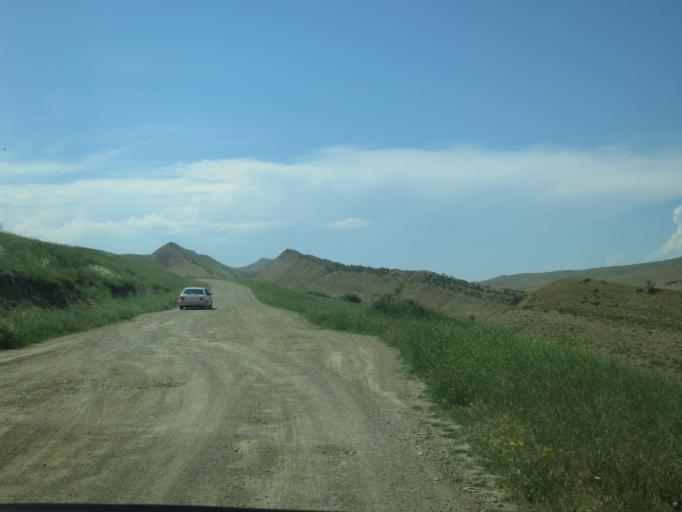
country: AZ
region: Agstafa
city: Saloglu
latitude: 41.4580
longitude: 45.3595
